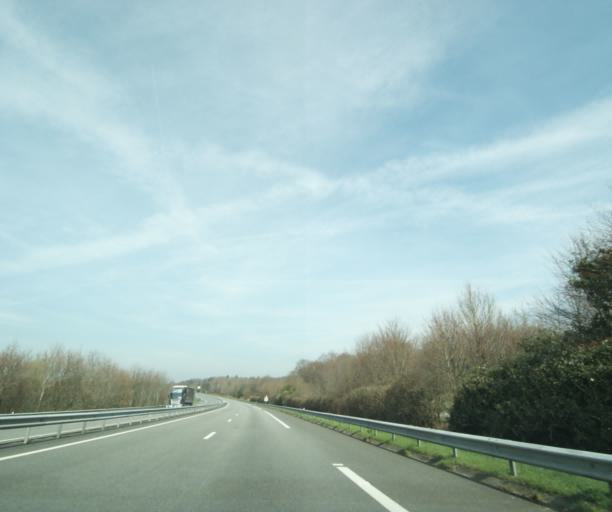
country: FR
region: Limousin
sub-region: Departement de la Haute-Vienne
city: Saint-Germain-les-Belles
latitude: 45.5193
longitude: 1.5169
